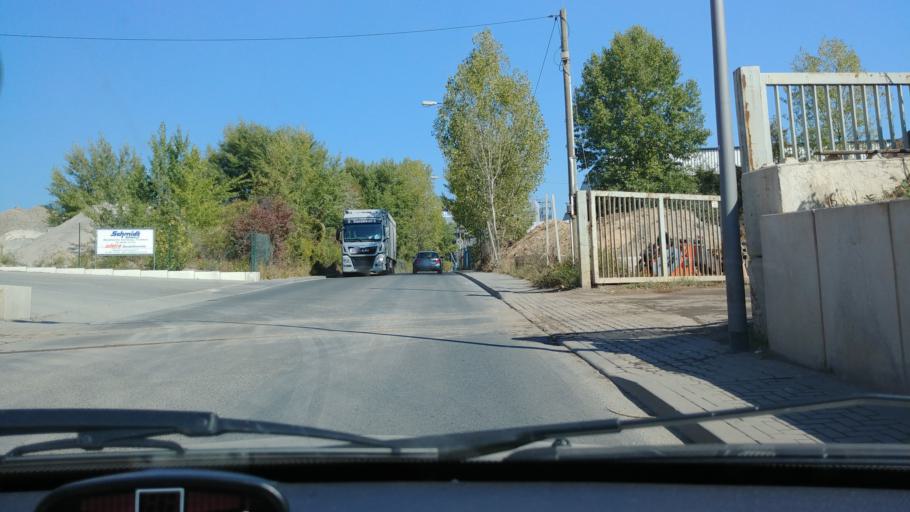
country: DE
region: Hesse
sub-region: Regierungsbezirk Darmstadt
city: Wiesbaden
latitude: 50.0419
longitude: 8.2597
